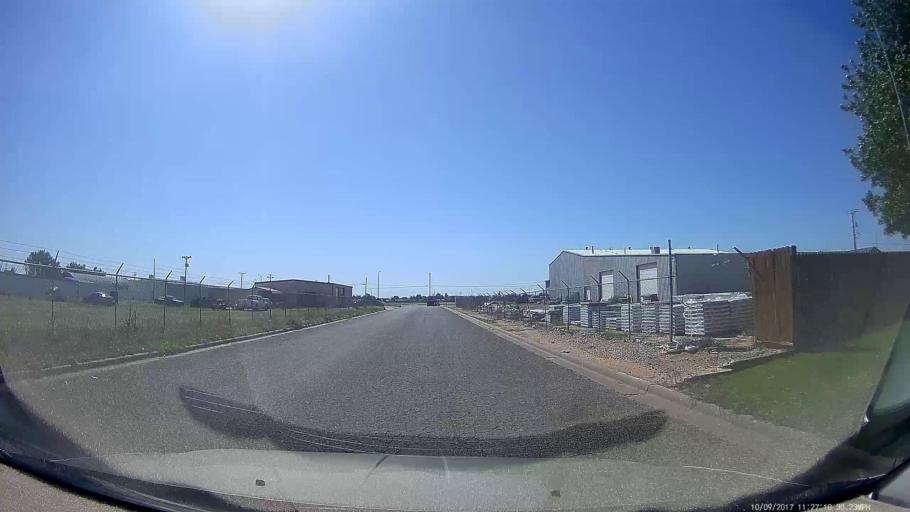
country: US
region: New Mexico
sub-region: Curry County
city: Clovis
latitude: 34.4055
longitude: -103.2273
